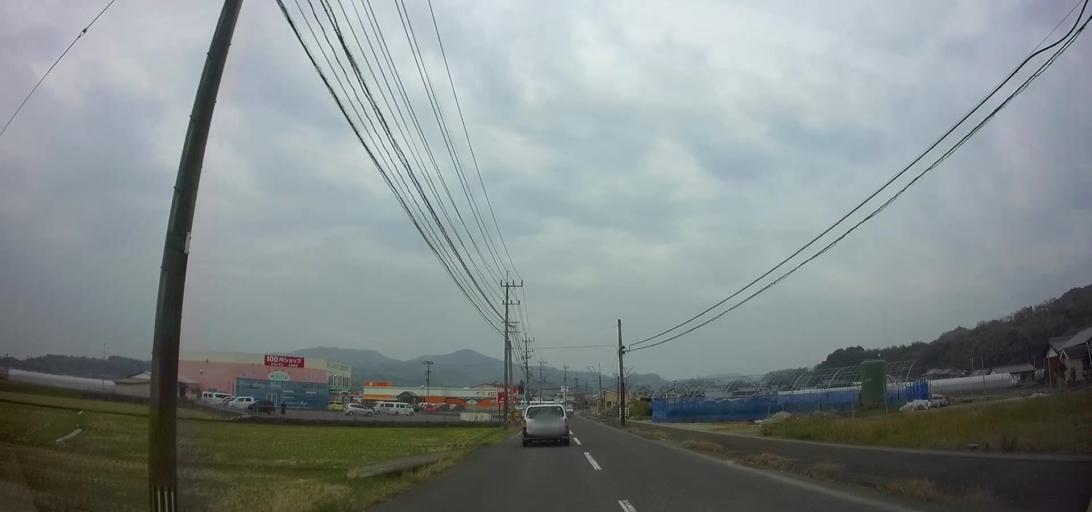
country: JP
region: Nagasaki
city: Shimabara
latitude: 32.6562
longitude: 130.2557
